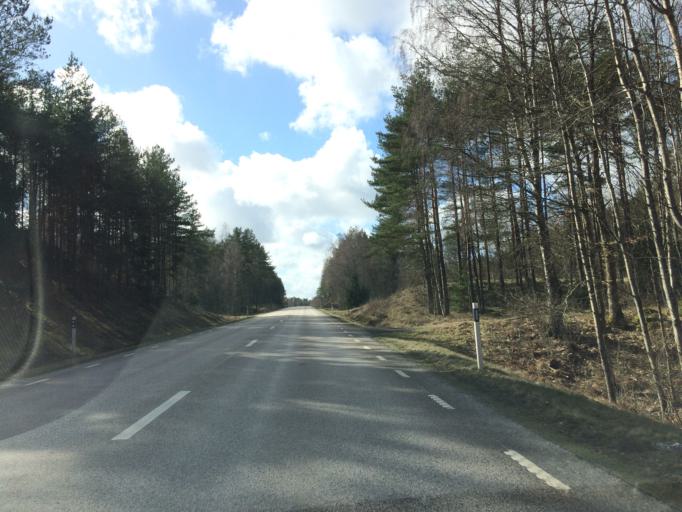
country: SE
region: Halland
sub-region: Laholms Kommun
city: Knared
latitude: 56.4919
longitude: 13.4371
